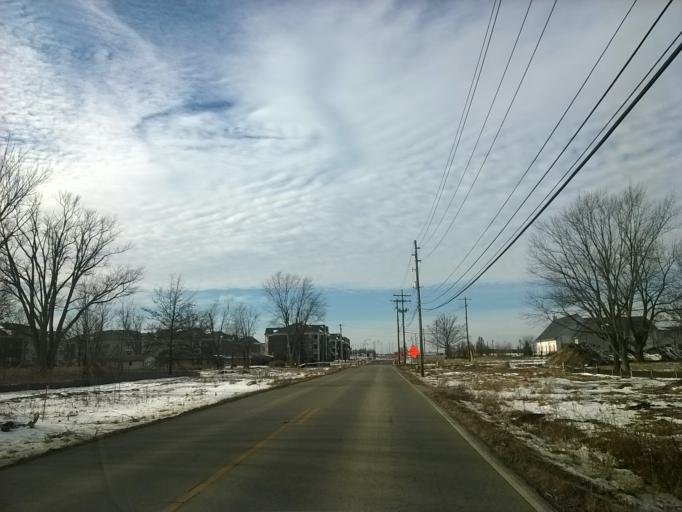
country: US
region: Indiana
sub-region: Hamilton County
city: Carmel
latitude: 39.9780
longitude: -86.1504
